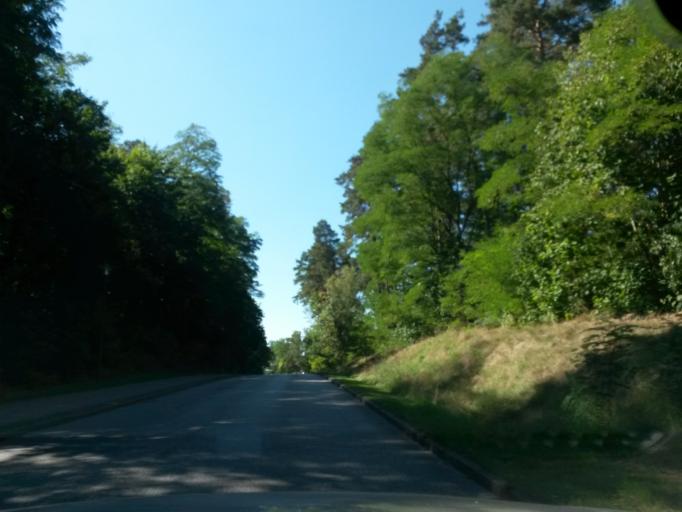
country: DE
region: Brandenburg
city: Lychen
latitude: 53.2185
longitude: 13.3170
